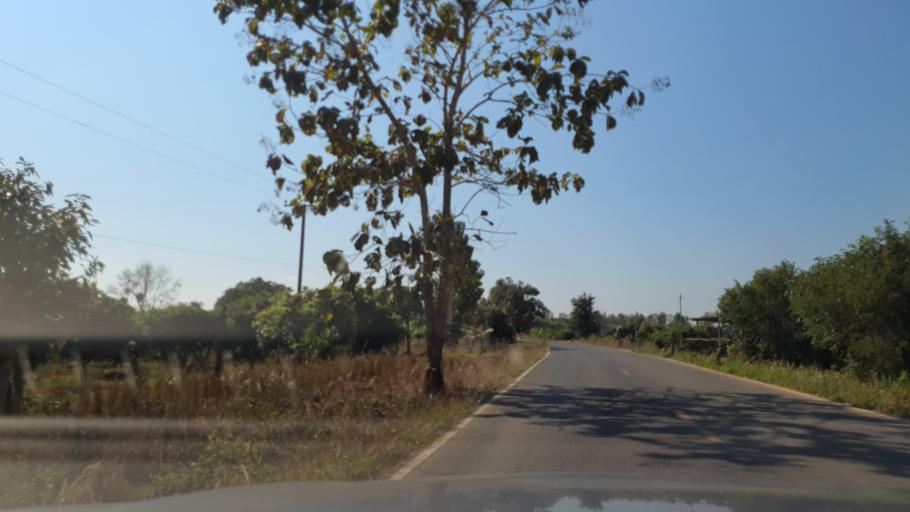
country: TH
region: Nan
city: Pua
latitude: 19.1273
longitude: 100.9226
